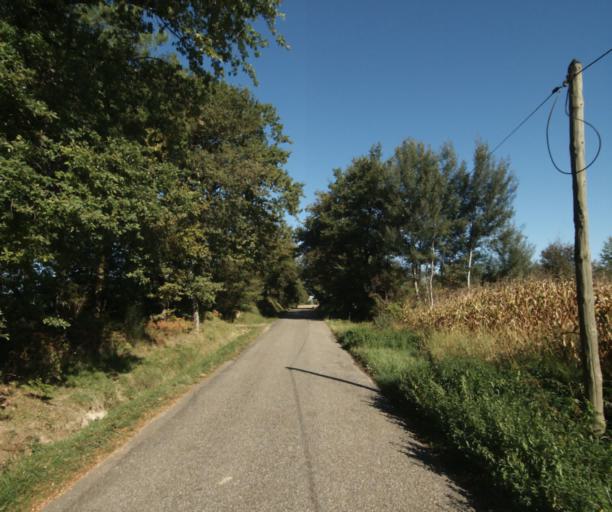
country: FR
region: Midi-Pyrenees
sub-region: Departement du Gers
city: Eauze
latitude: 43.8194
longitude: 0.1249
